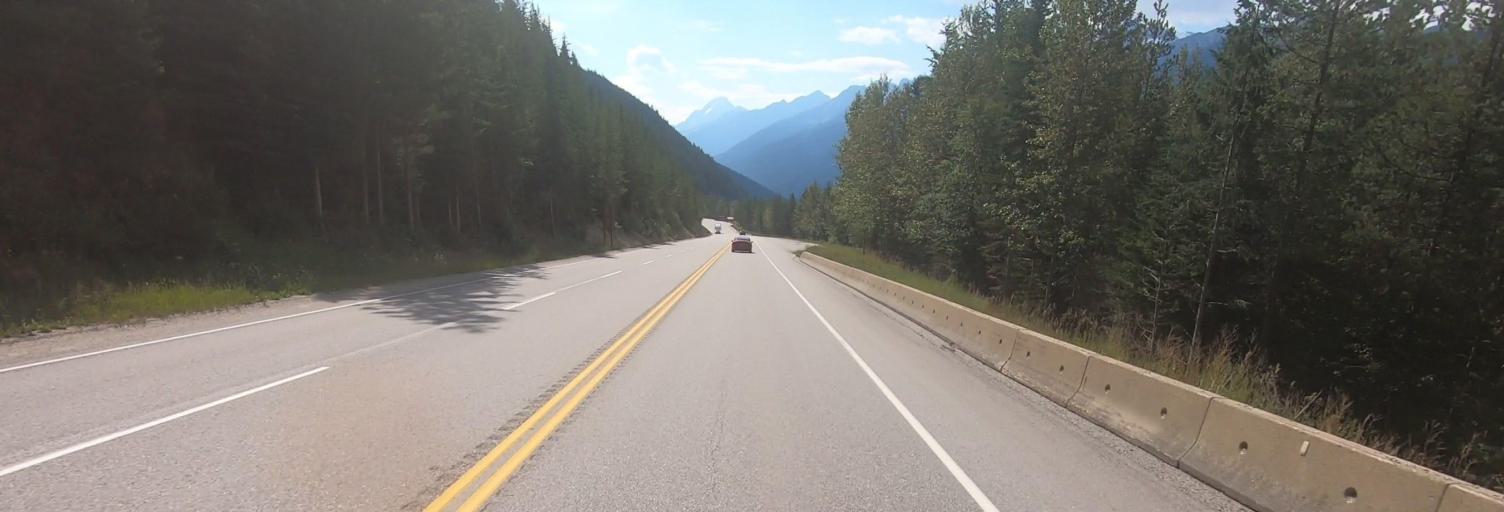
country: CA
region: British Columbia
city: Golden
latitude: 51.4683
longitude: -117.4813
